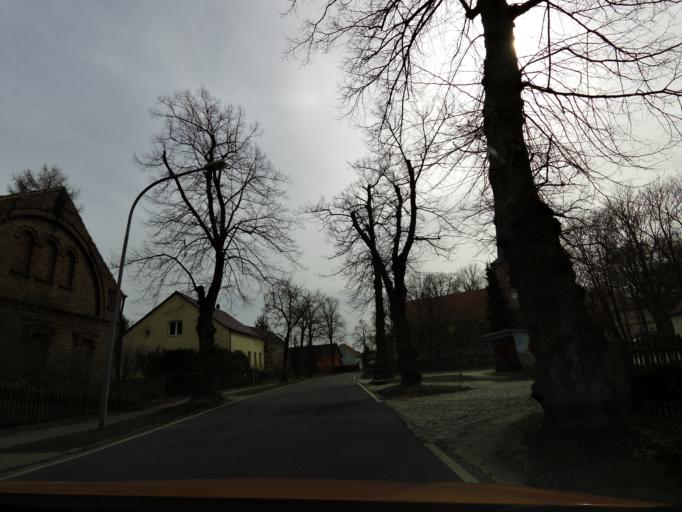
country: DE
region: Brandenburg
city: Rangsdorf
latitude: 52.3012
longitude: 13.3838
